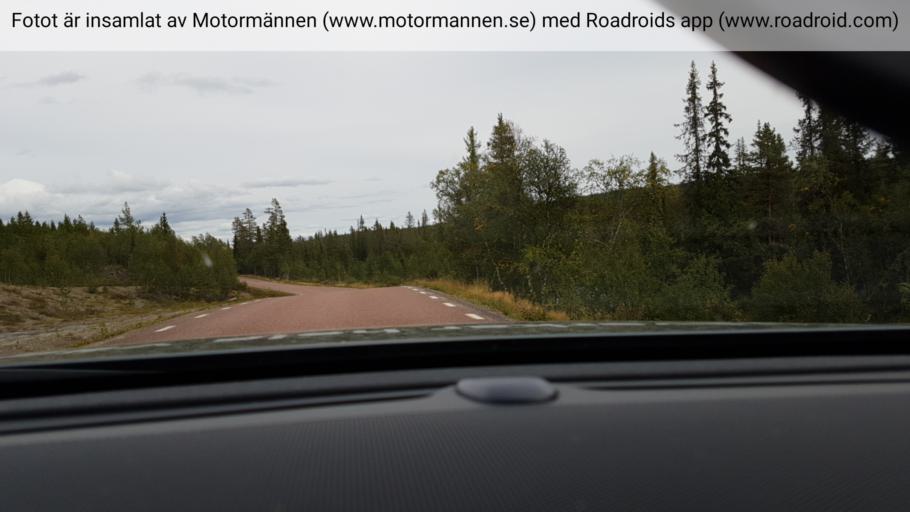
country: NO
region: Hedmark
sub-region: Trysil
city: Innbygda
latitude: 61.6881
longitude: 12.5457
